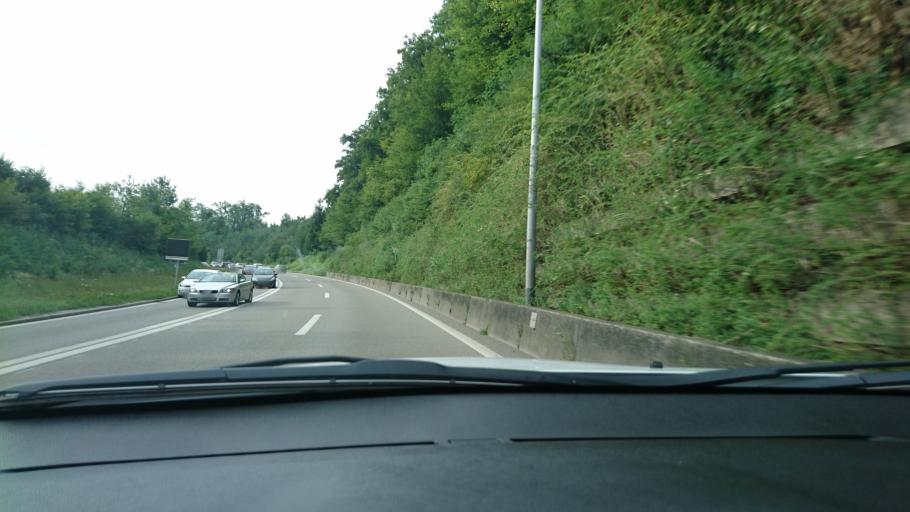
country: CH
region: Zurich
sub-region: Bezirk Uster
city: Uster / Ober-Uster
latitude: 47.3472
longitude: 8.7434
